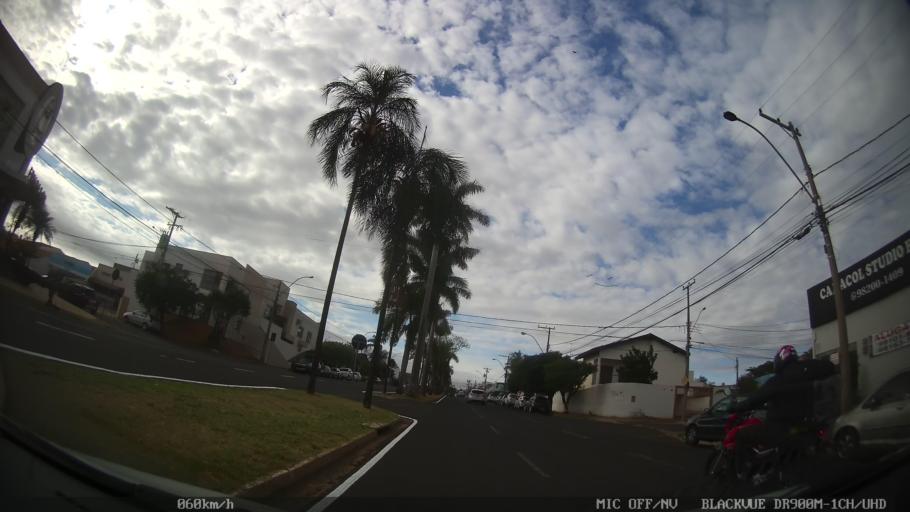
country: BR
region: Sao Paulo
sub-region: Sao Jose Do Rio Preto
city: Sao Jose do Rio Preto
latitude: -20.8323
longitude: -49.4015
